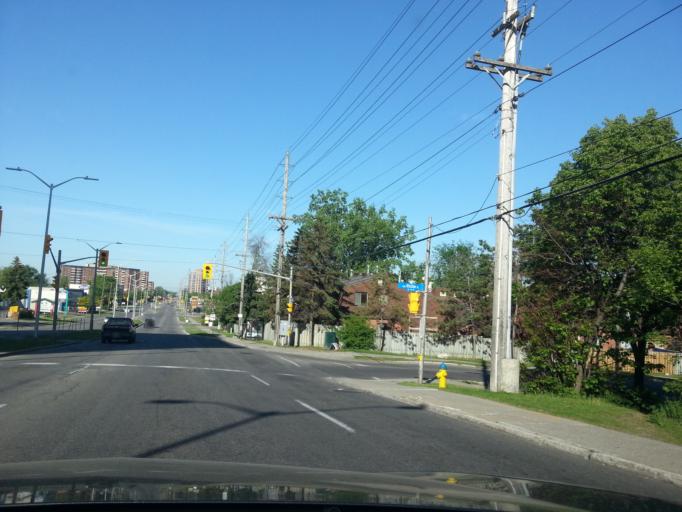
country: CA
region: Ontario
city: Bells Corners
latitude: 45.3573
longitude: -75.8003
